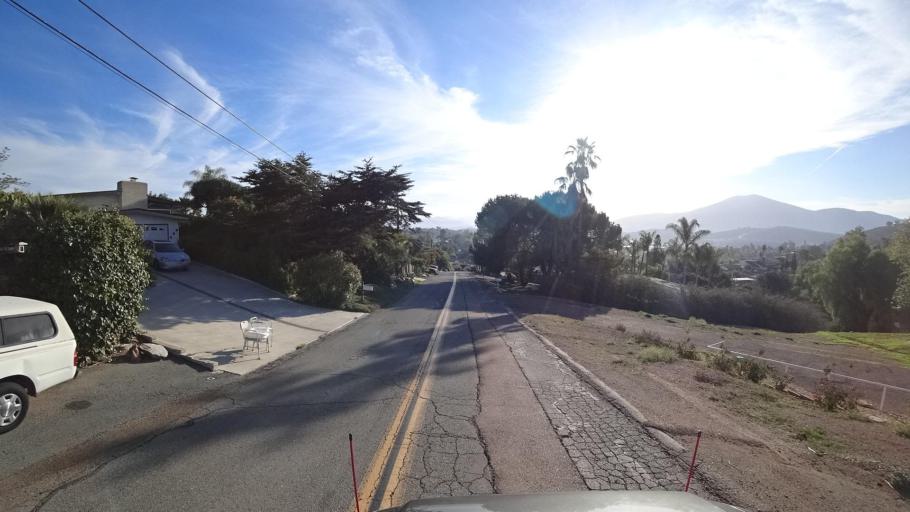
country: US
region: California
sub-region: San Diego County
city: Spring Valley
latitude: 32.7364
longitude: -116.9852
